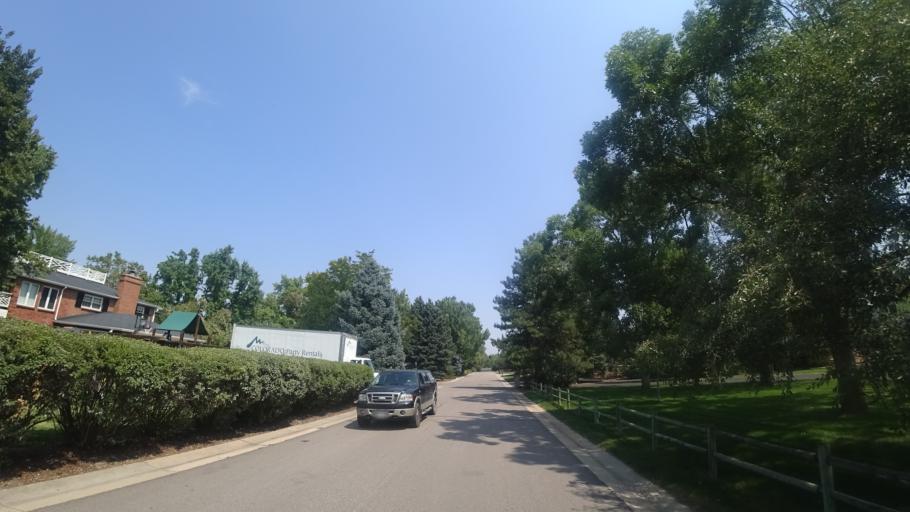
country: US
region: Colorado
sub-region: Arapahoe County
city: Greenwood Village
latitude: 39.6213
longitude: -104.9747
